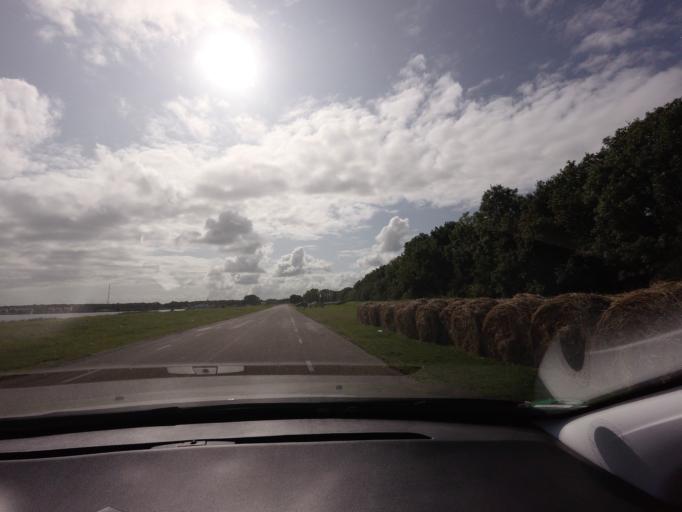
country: NL
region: North Holland
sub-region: Gemeente Hollands Kroon
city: Den Oever
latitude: 52.9282
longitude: 5.0378
